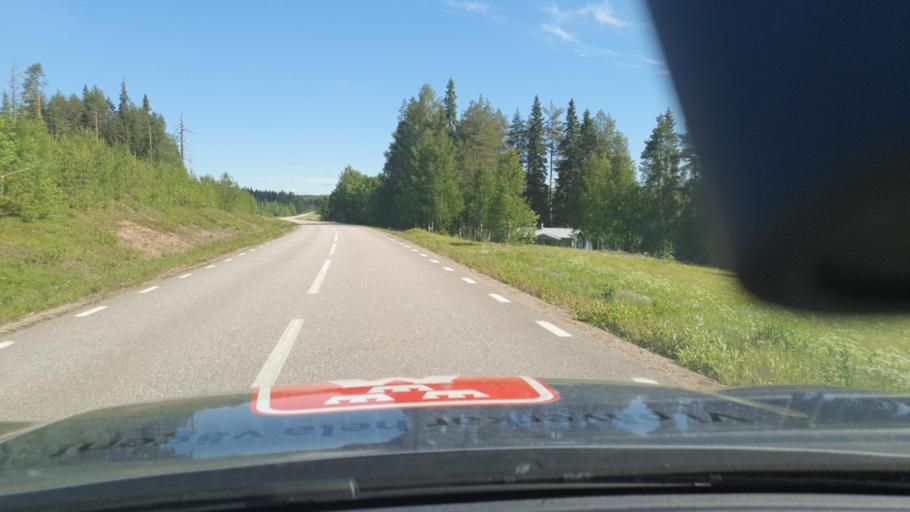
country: SE
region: Norrbotten
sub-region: Overkalix Kommun
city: OEverkalix
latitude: 66.7691
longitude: 22.6887
